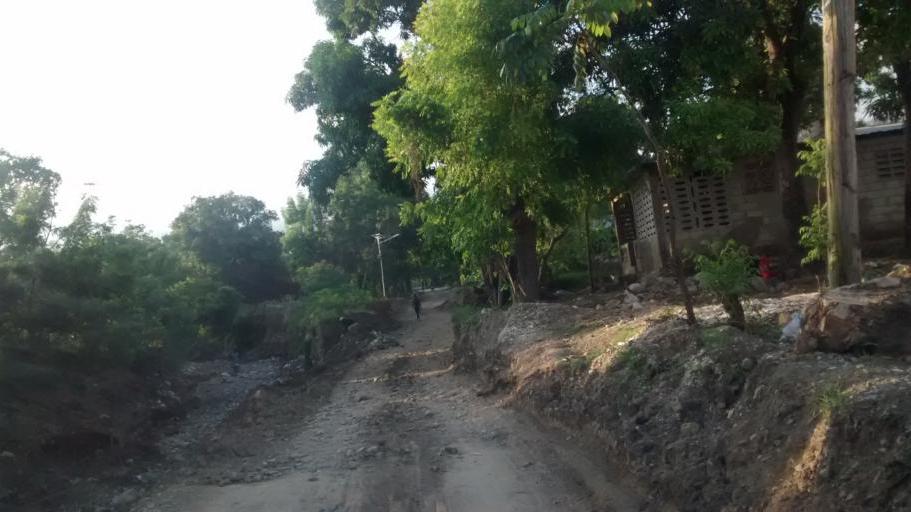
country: HT
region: Ouest
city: Grangwav
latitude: 18.4255
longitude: -72.7831
